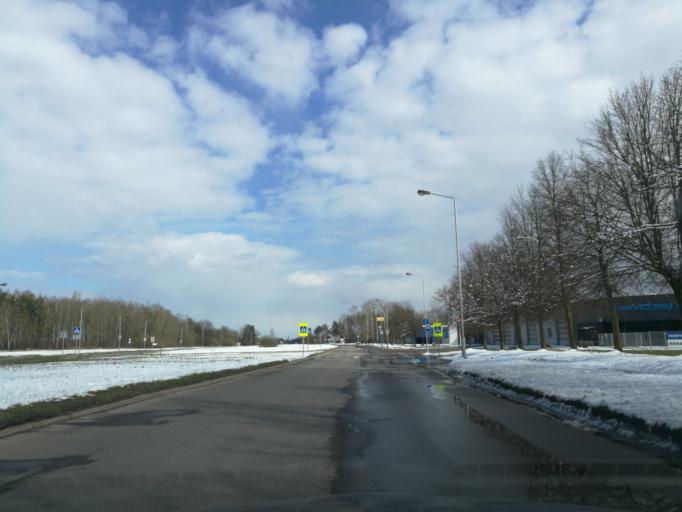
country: LT
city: Ramuciai
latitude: 54.9180
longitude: 24.0224
